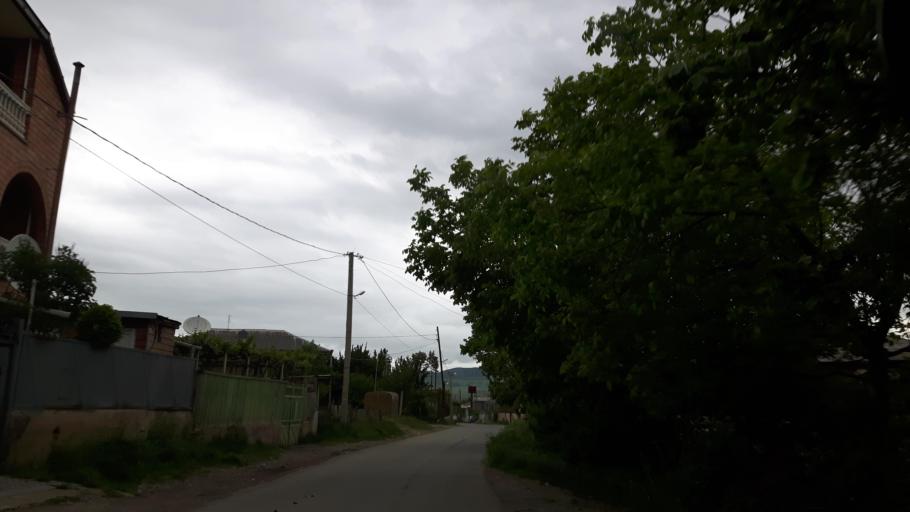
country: GE
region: Shida Kartli
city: Gori
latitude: 41.9440
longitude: 44.1208
